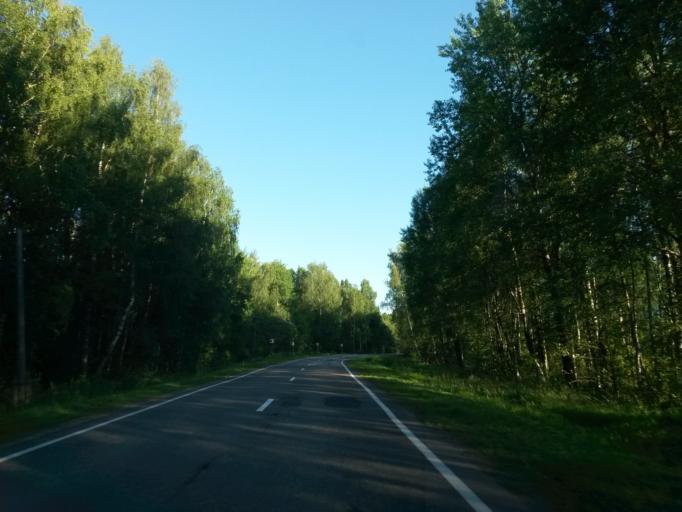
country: RU
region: Jaroslavl
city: Tutayev
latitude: 57.9221
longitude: 39.5121
